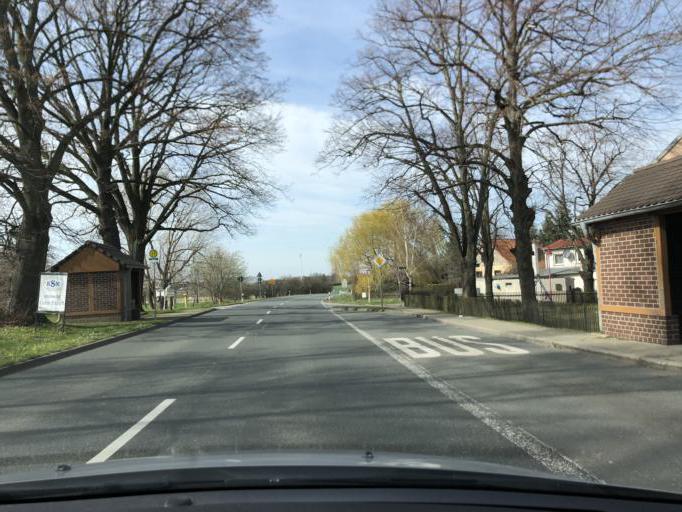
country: DE
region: Saxony-Anhalt
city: Osterfeld
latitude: 51.0862
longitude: 11.9650
